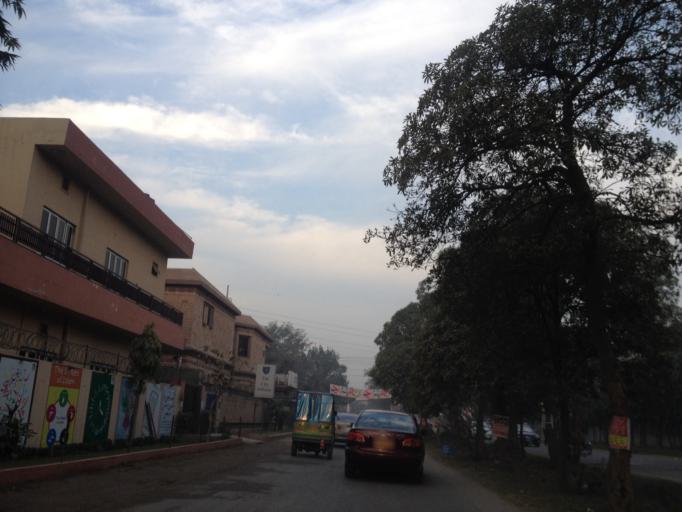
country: PK
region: Punjab
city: Lahore
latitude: 31.4601
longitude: 74.3002
